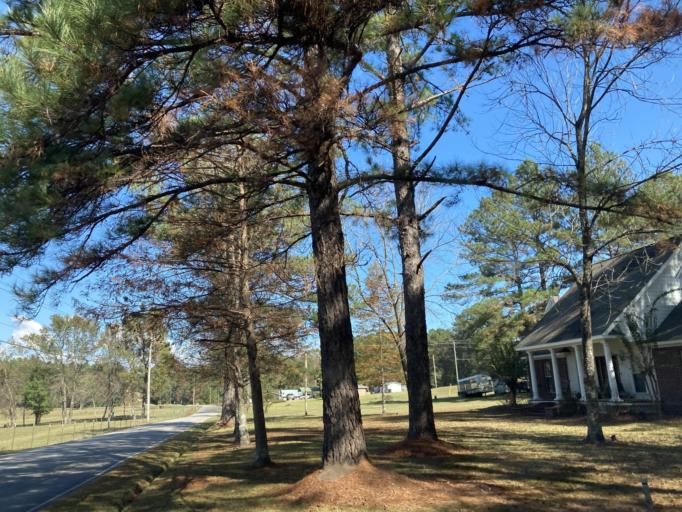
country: US
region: Mississippi
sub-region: Lamar County
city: West Hattiesburg
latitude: 31.2589
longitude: -89.4342
